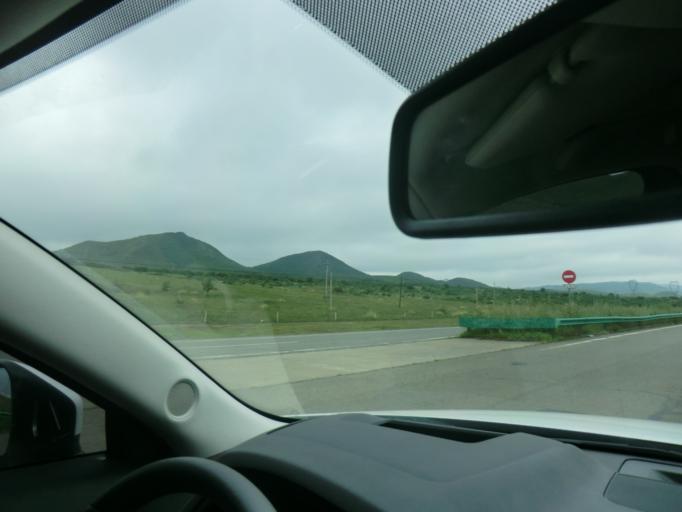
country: CN
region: Inner Mongolia
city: Bayart Huxu
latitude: 45.1133
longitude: 120.1017
